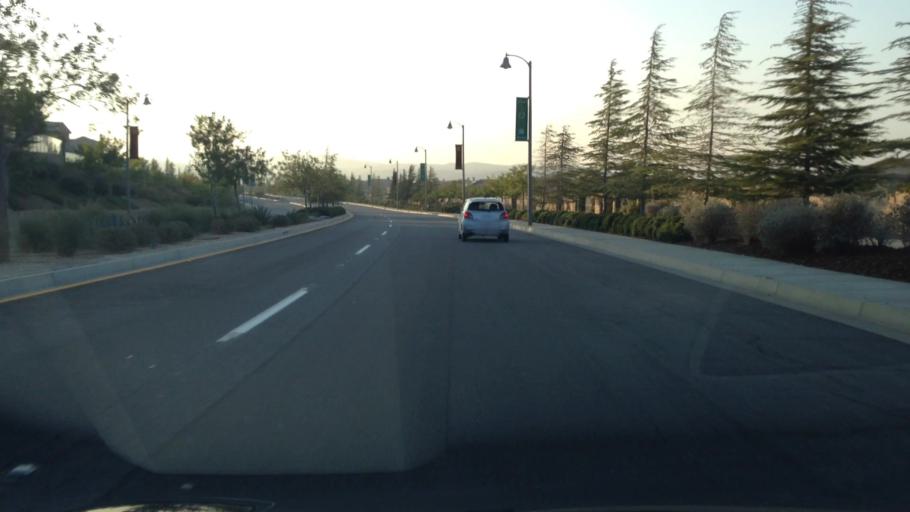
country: US
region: California
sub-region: Los Angeles County
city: Desert View Highlands
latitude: 34.5628
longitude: -118.1695
